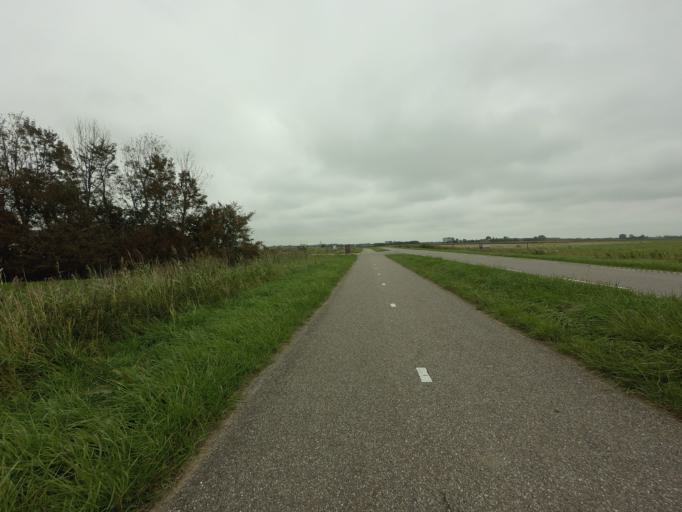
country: NL
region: Zeeland
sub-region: Gemeente Middelburg
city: Middelburg
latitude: 51.5070
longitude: 3.5636
